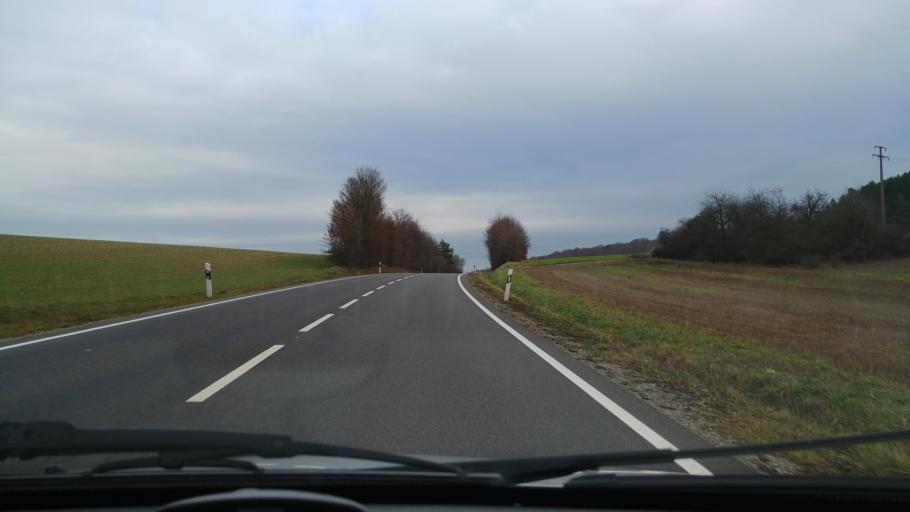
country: DE
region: Bavaria
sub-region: Regierungsbezirk Unterfranken
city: Karlstadt
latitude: 49.9599
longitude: 9.7963
